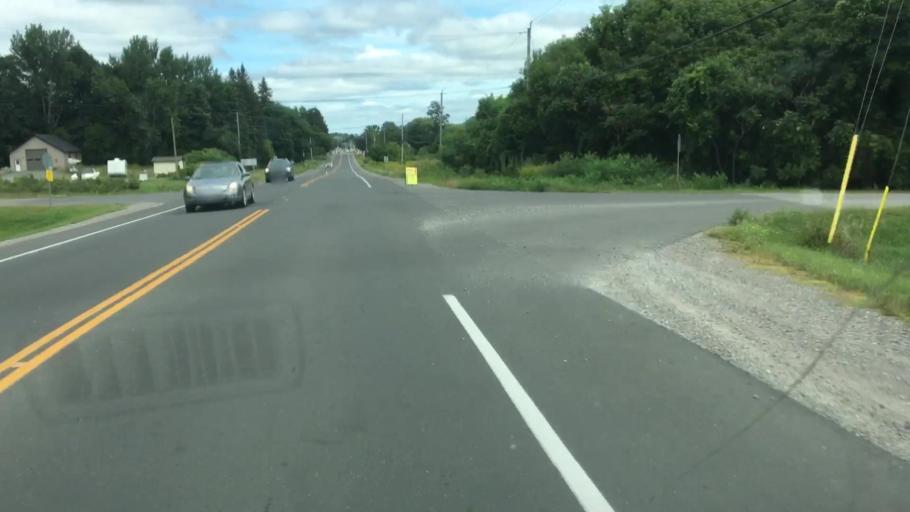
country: CA
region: Ontario
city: Quinte West
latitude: 44.0352
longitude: -77.7665
